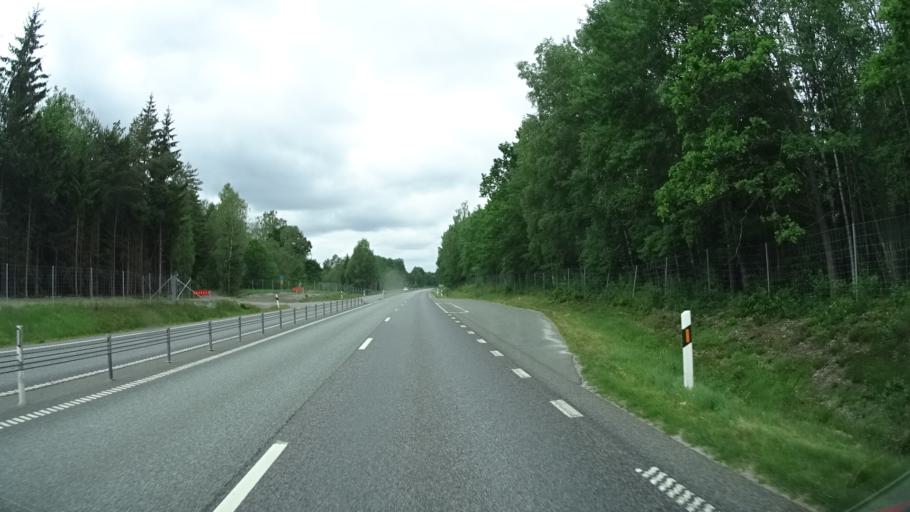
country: SE
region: Kronoberg
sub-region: Ljungby Kommun
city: Lagan
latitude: 56.8511
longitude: 14.0302
